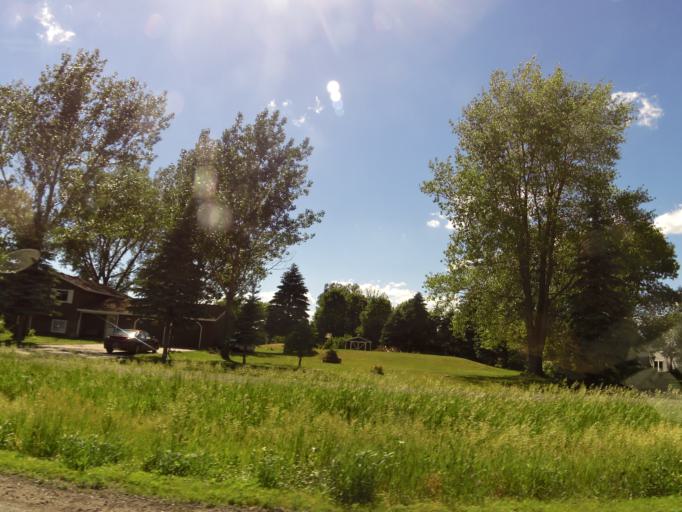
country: US
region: Minnesota
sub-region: Stearns County
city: Saint Augusta
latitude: 45.4730
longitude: -94.2463
